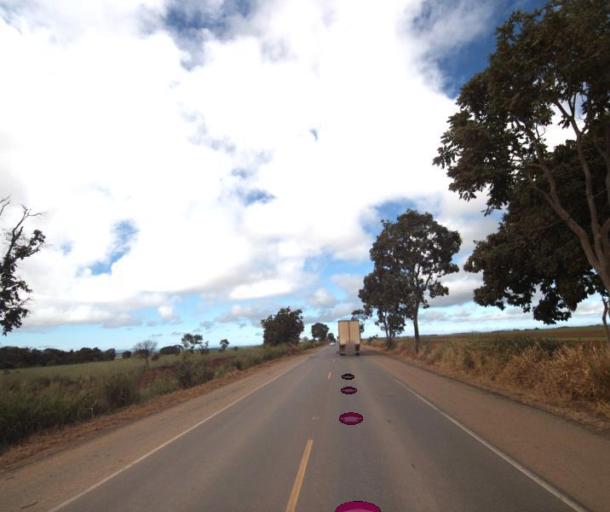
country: BR
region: Goias
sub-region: Uruacu
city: Uruacu
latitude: -14.7641
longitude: -49.2619
